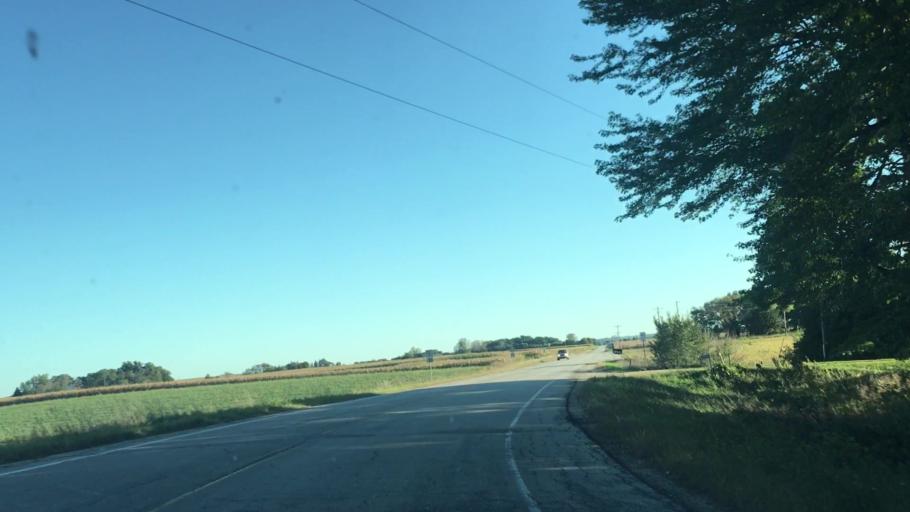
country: US
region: Minnesota
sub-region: Fillmore County
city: Chatfield
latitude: 43.8349
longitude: -92.0693
